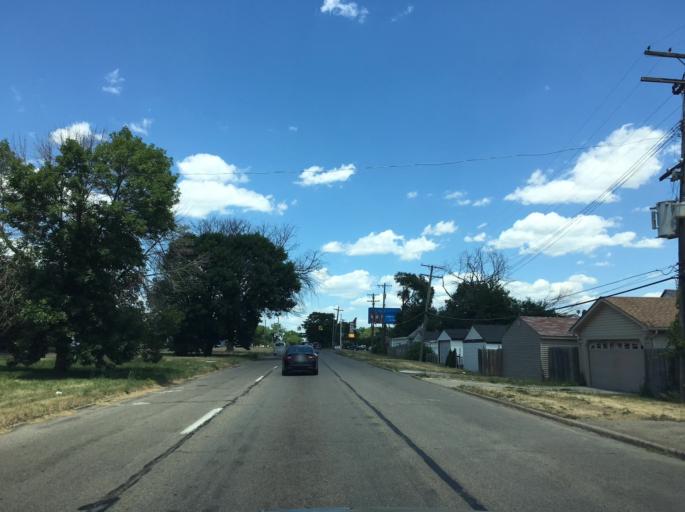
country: US
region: Michigan
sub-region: Wayne County
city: Hamtramck
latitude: 42.4322
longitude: -83.0433
